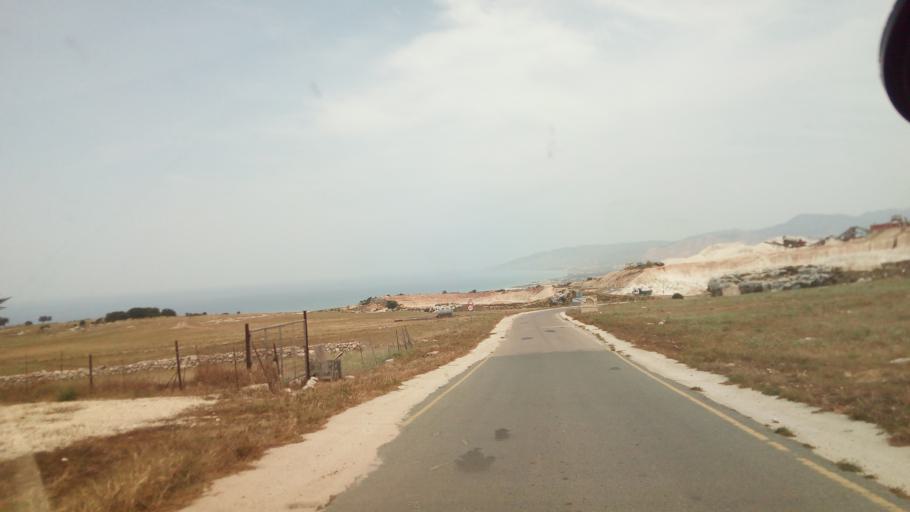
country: CY
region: Pafos
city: Polis
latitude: 35.0007
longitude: 32.3833
